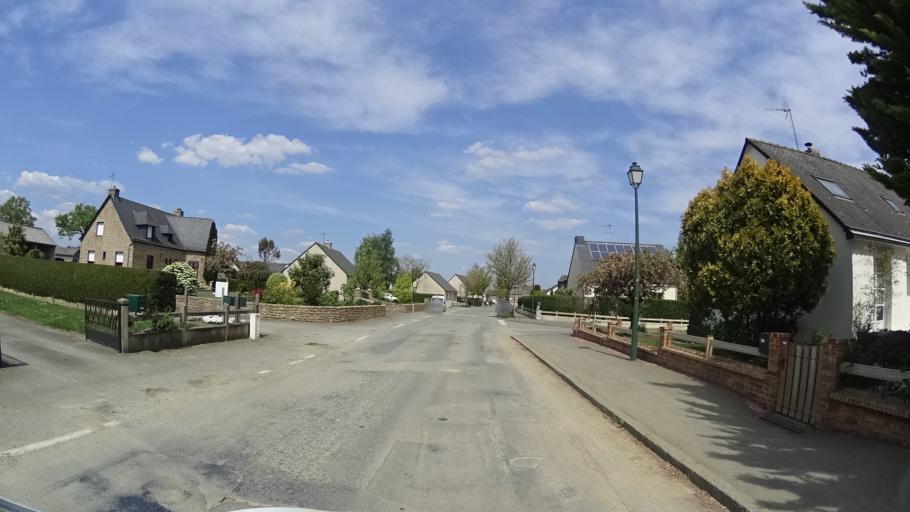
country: FR
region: Brittany
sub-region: Departement d'Ille-et-Vilaine
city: Torce
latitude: 48.0597
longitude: -1.2682
